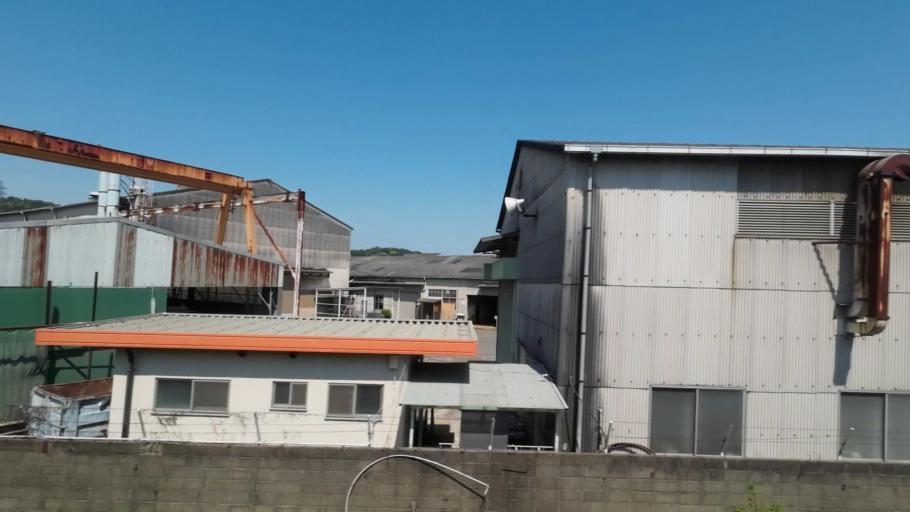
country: JP
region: Ehime
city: Niihama
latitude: 33.9418
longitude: 133.2876
